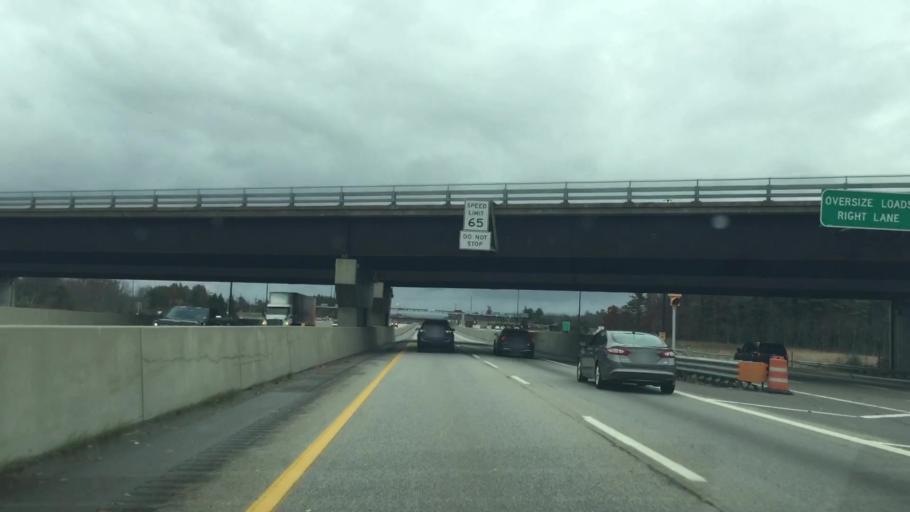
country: US
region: New Hampshire
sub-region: Rockingham County
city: Hampton
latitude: 42.9591
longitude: -70.8570
